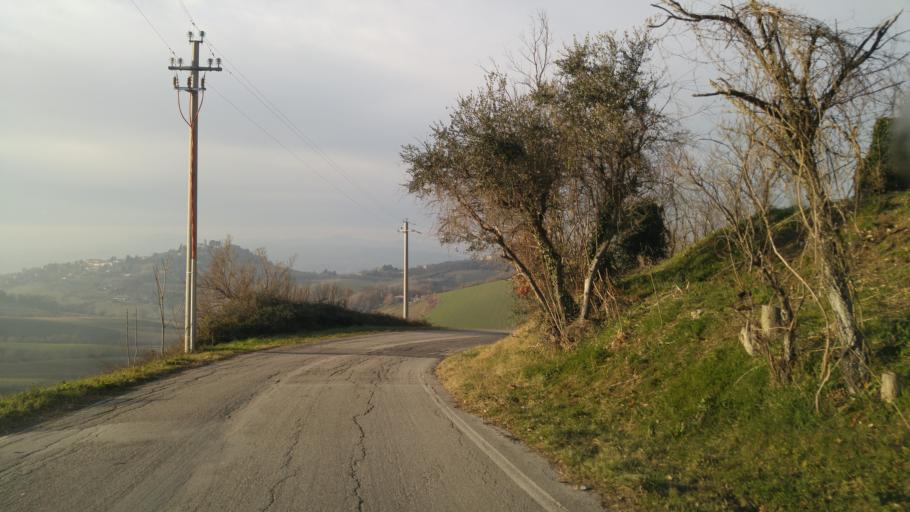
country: IT
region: The Marches
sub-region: Provincia di Pesaro e Urbino
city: Piagge
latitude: 43.7327
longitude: 12.9658
